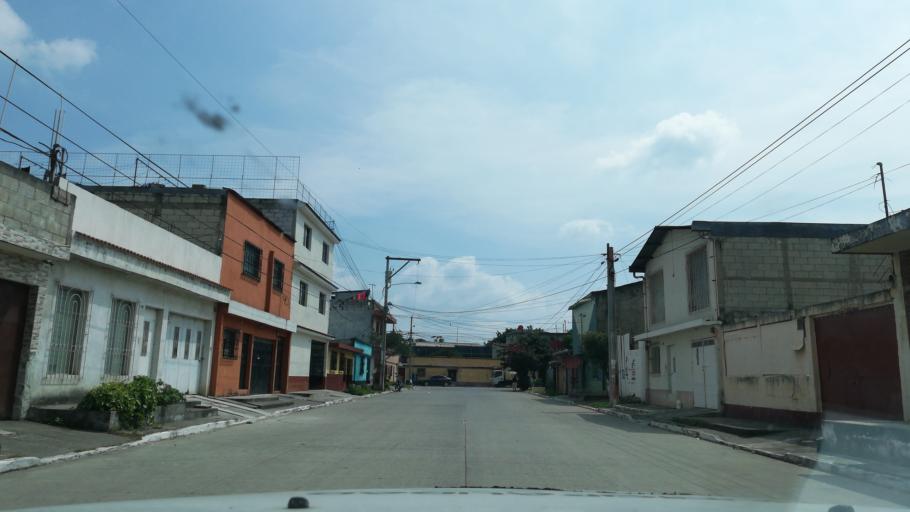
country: GT
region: Guatemala
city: Petapa
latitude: 14.5047
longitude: -90.5654
